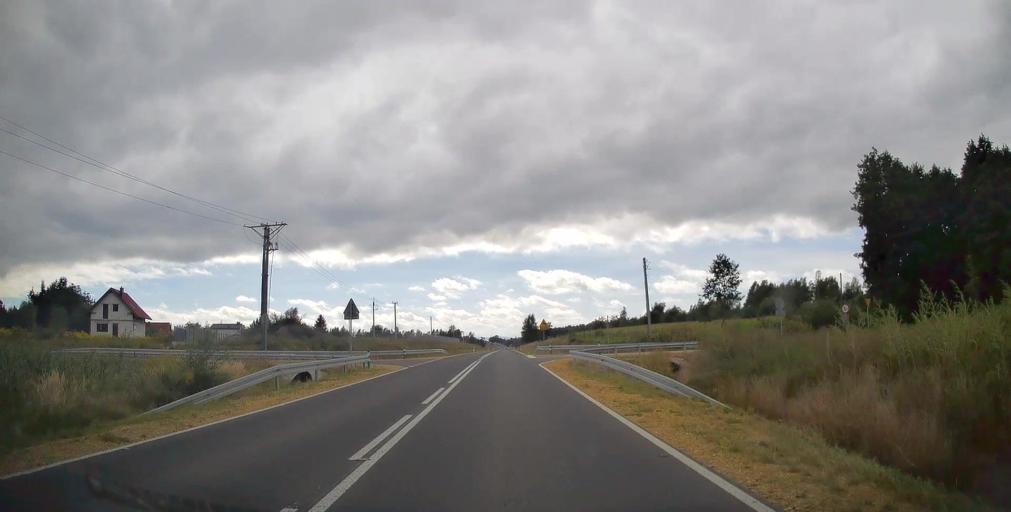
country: PL
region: Lesser Poland Voivodeship
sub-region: Powiat oswiecimski
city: Zator
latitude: 50.0118
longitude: 19.4258
